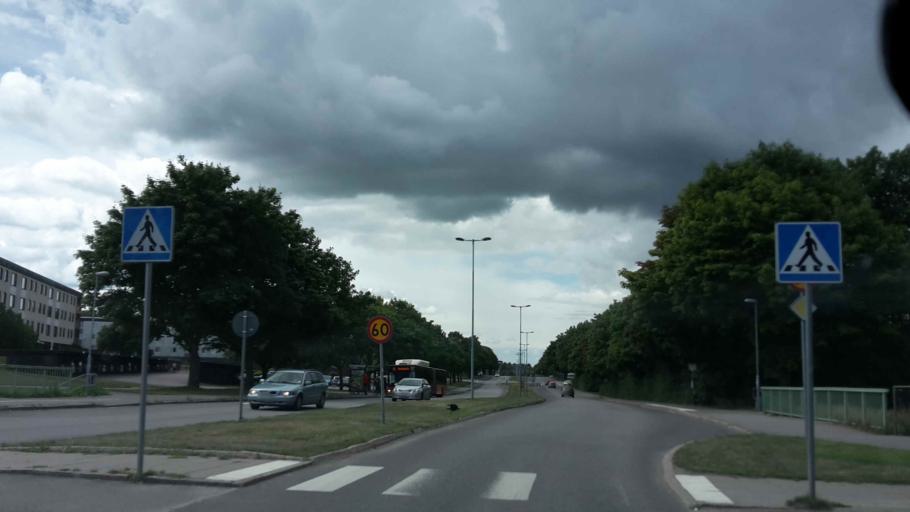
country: SE
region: OEstergoetland
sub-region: Norrkopings Kommun
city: Norrkoping
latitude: 58.5809
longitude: 16.1703
